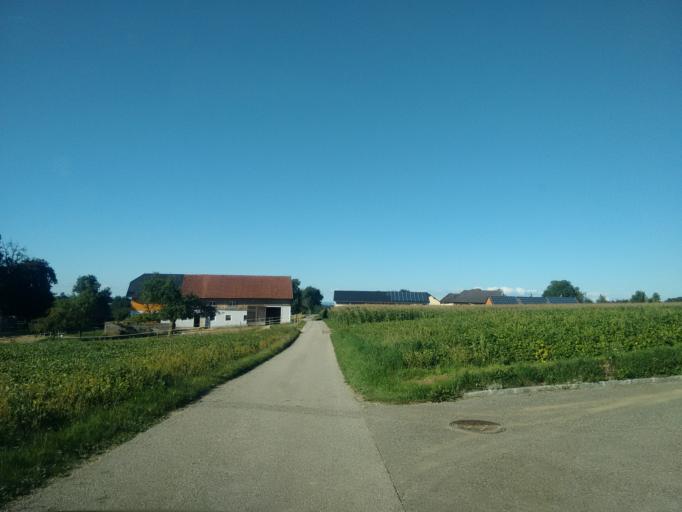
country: AT
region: Upper Austria
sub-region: Politischer Bezirk Kirchdorf an der Krems
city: Kremsmunster
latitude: 48.0787
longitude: 14.0993
